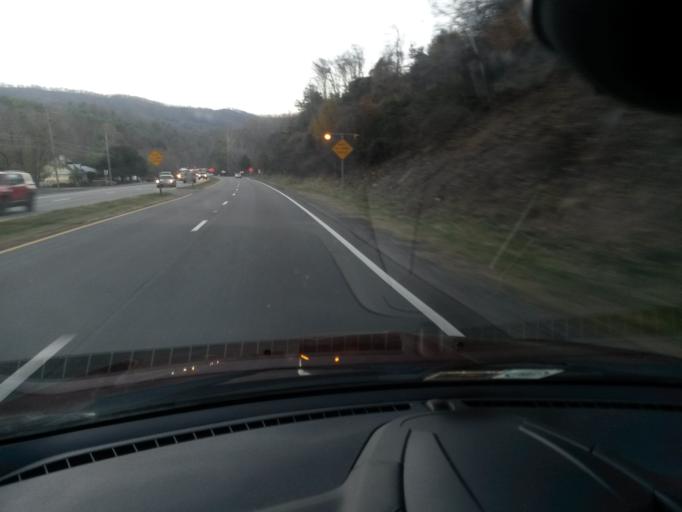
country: US
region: Virginia
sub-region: Roanoke County
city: Narrows
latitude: 37.1863
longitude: -79.9364
